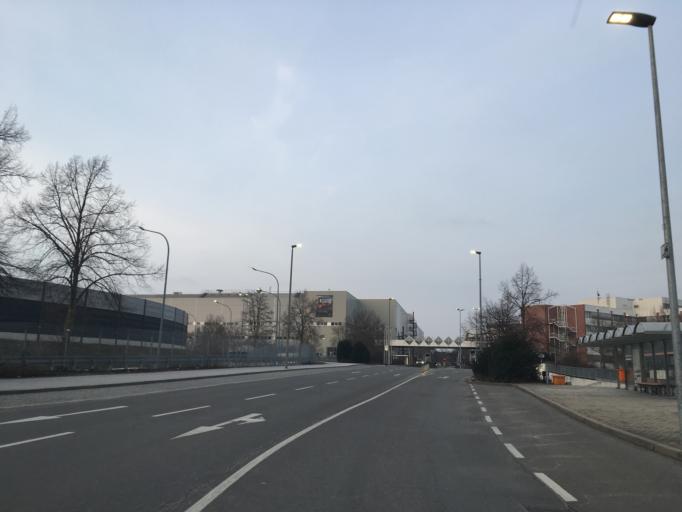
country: DE
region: Baden-Wuerttemberg
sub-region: Regierungsbezirk Stuttgart
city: Sindelfingen
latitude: 48.6980
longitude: 9.0014
